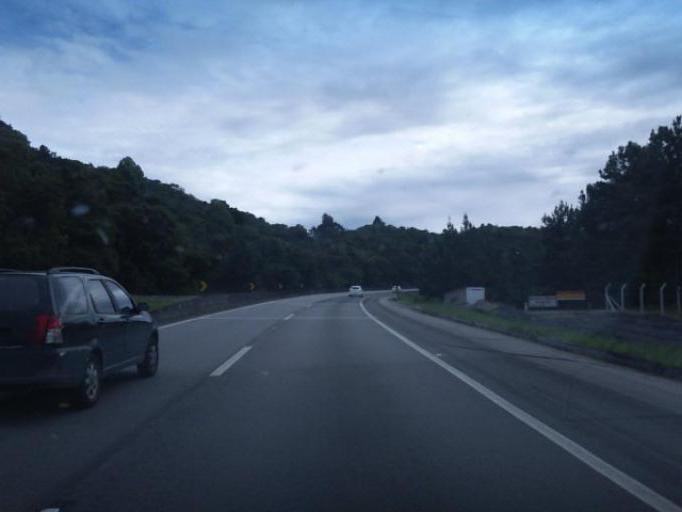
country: BR
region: Parana
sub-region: Campina Grande Do Sul
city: Campina Grande do Sul
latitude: -25.1730
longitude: -48.8680
